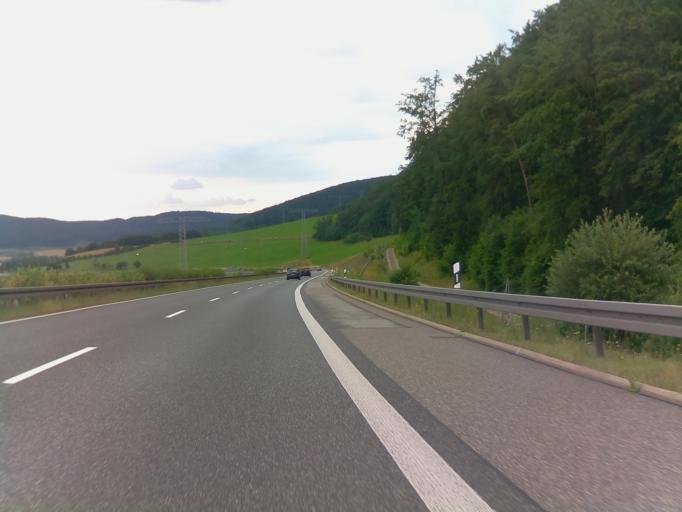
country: DE
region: Thuringia
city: Ellingshausen
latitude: 50.5640
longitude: 10.4783
